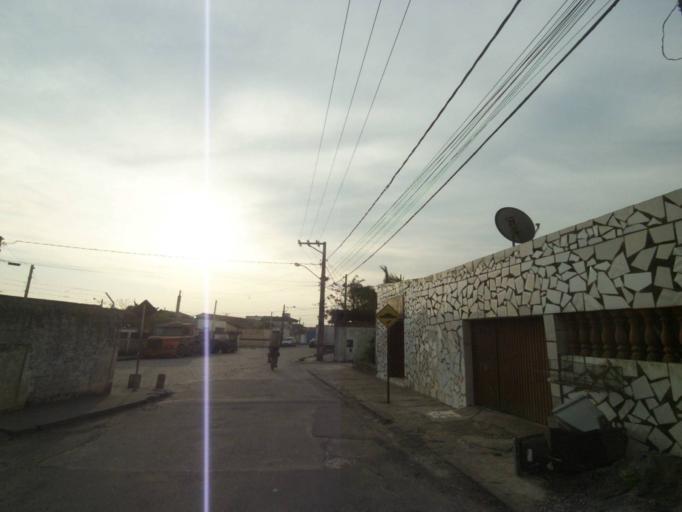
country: BR
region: Parana
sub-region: Paranagua
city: Paranagua
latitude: -25.5279
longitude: -48.5330
